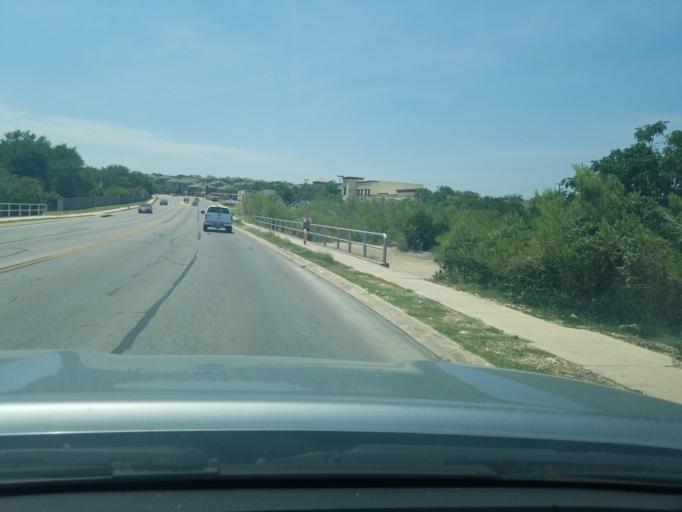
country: US
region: Texas
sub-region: Bexar County
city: Timberwood Park
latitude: 29.6849
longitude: -98.4709
